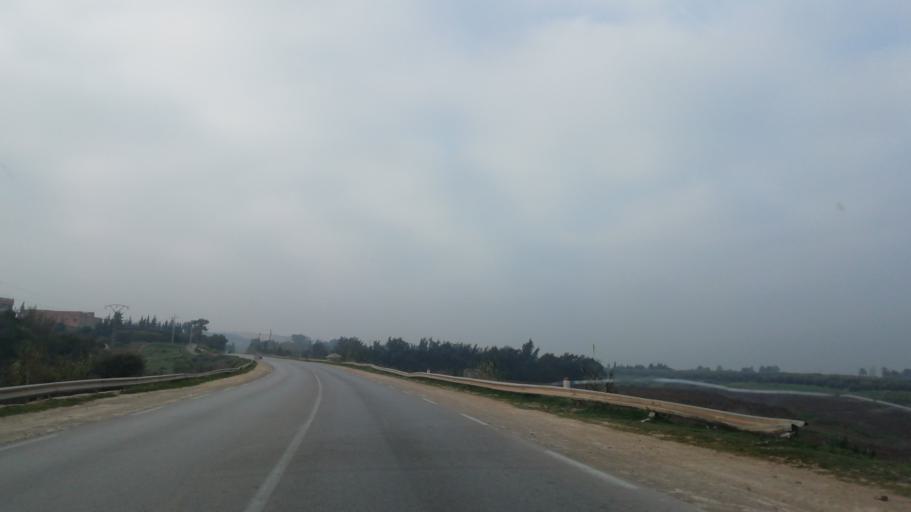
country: DZ
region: Relizane
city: Djidiouia
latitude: 35.9359
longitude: 0.8521
